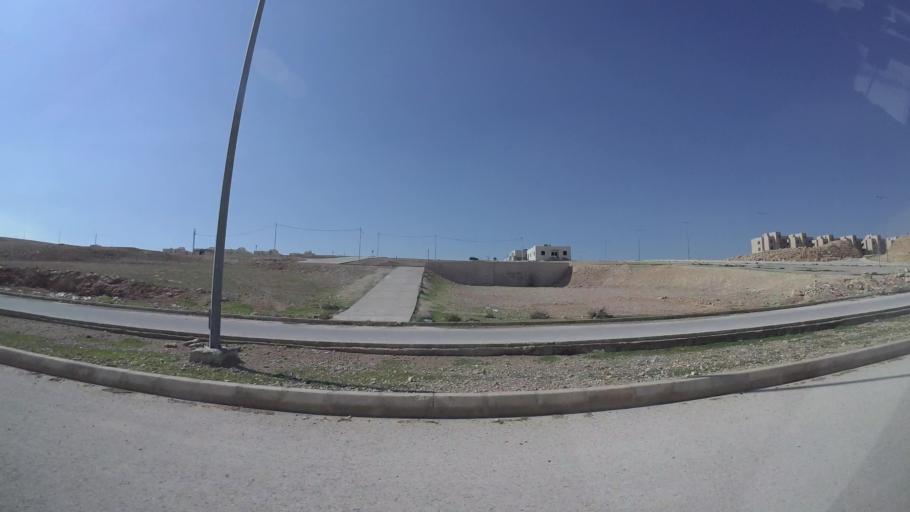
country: JO
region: Zarqa
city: Zarqa
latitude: 32.0537
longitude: 36.1251
